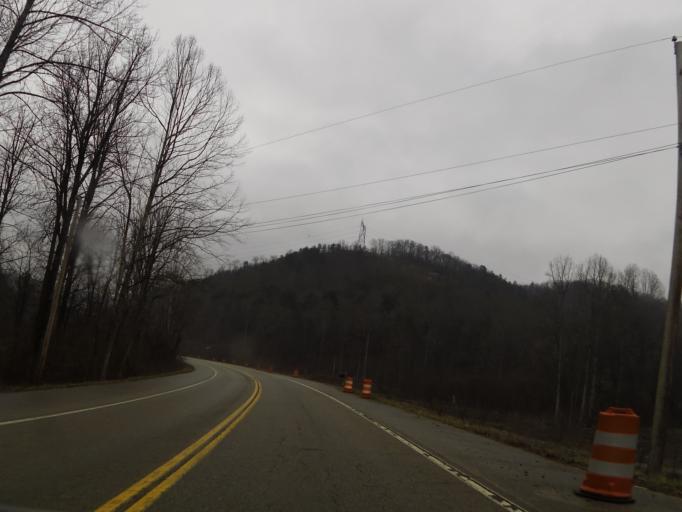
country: US
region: Tennessee
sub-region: Morgan County
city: Coalfield
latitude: 35.9800
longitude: -84.4817
